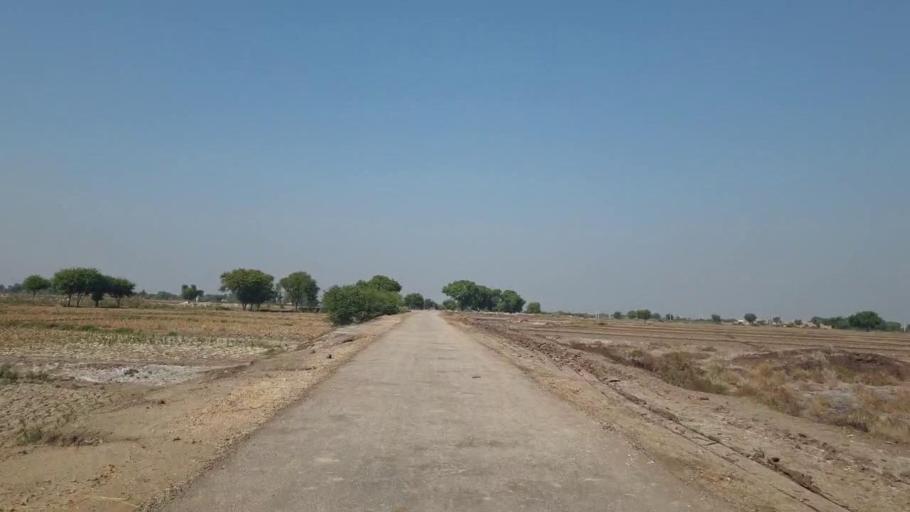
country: PK
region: Sindh
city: Sehwan
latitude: 26.4262
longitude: 67.8298
